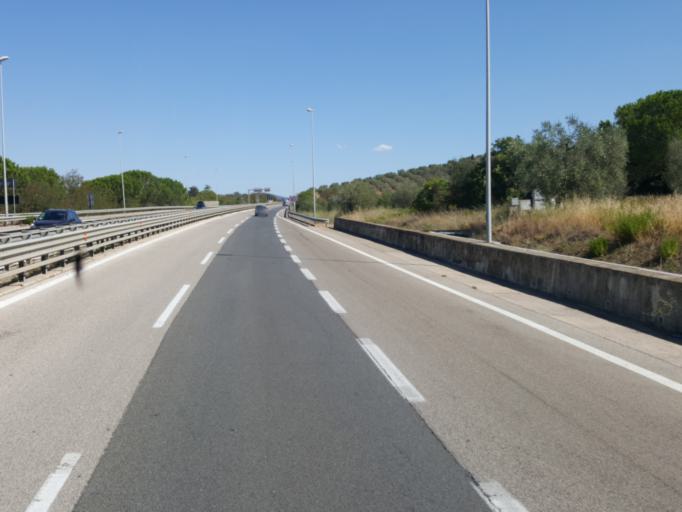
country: IT
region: Tuscany
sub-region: Provincia di Grosseto
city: Grosseto
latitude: 42.7316
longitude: 11.1359
